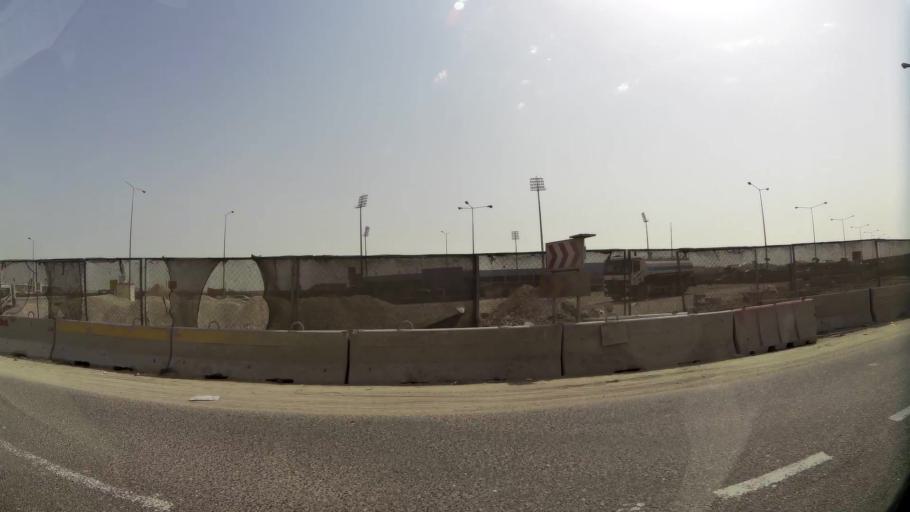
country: QA
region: Al Wakrah
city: Al Wukayr
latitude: 25.1893
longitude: 51.4572
